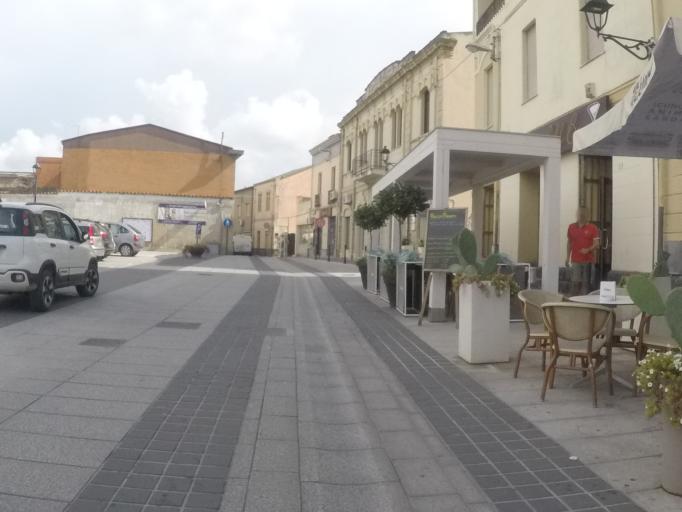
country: IT
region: Sardinia
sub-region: Provincia di Oristano
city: Terralba
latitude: 39.7201
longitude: 8.6366
